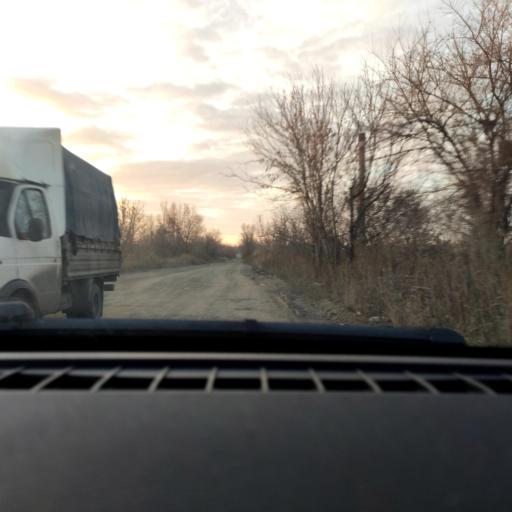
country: RU
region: Voronezj
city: Maslovka
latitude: 51.6133
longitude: 39.2675
